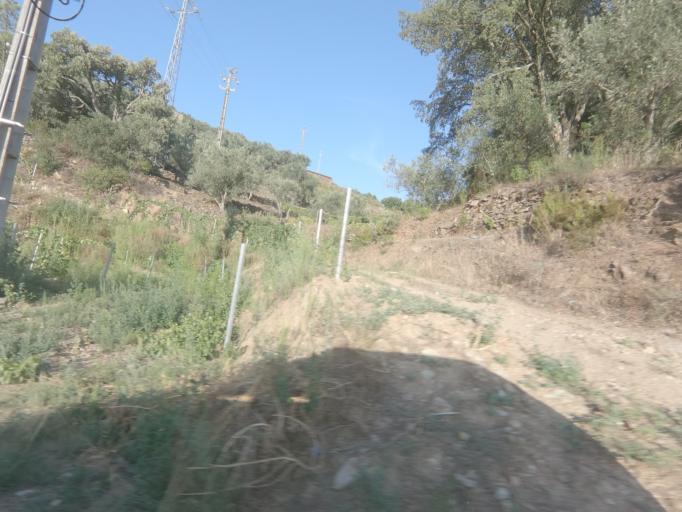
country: PT
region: Vila Real
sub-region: Sabrosa
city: Sabrosa
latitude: 41.2655
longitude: -7.5340
